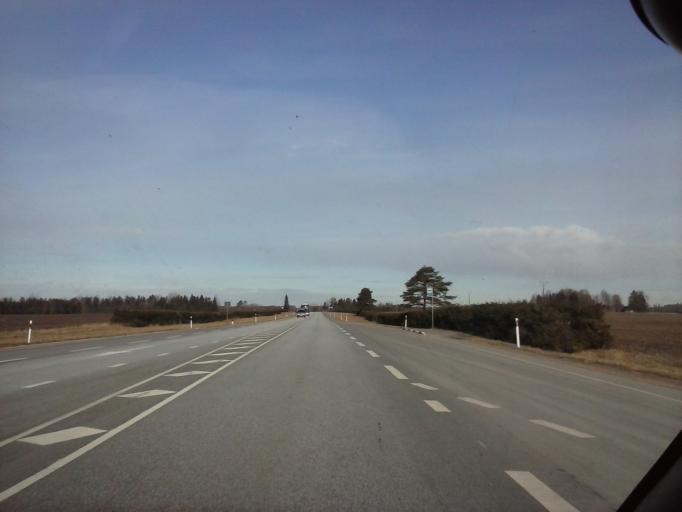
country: EE
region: Jogevamaa
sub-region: Poltsamaa linn
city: Poltsamaa
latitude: 58.7202
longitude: 25.8752
